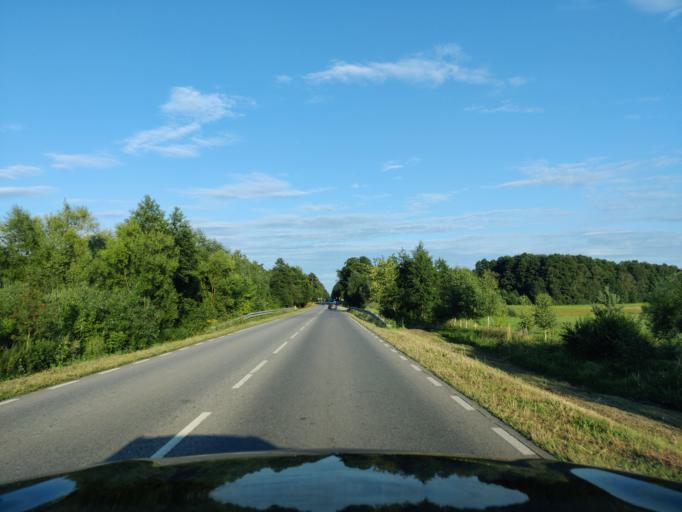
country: PL
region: Masovian Voivodeship
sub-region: Powiat pultuski
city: Pultusk
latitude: 52.6827
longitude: 21.1215
